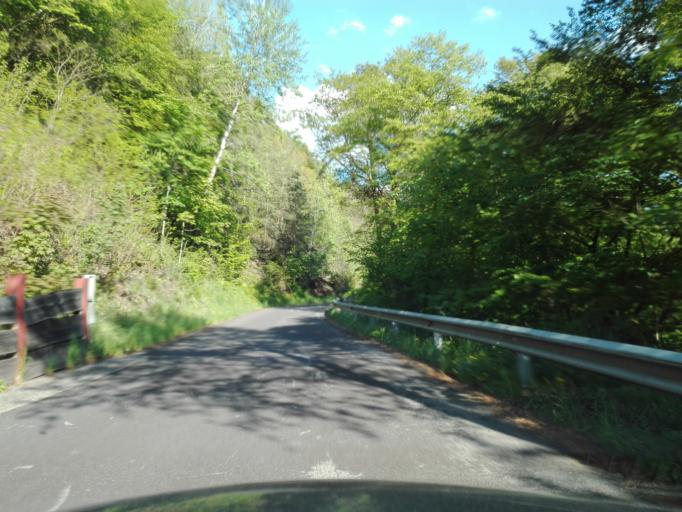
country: AT
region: Upper Austria
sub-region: Politischer Bezirk Rohrbach
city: Pfarrkirchen im Muehlkreis
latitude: 48.4612
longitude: 13.8175
